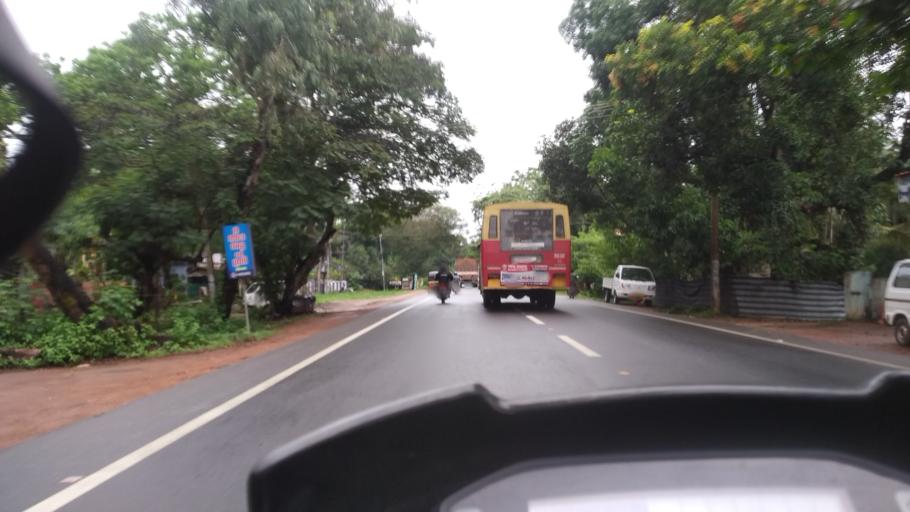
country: IN
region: Kerala
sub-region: Alappuzha
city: Mavelikara
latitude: 9.2903
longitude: 76.4366
